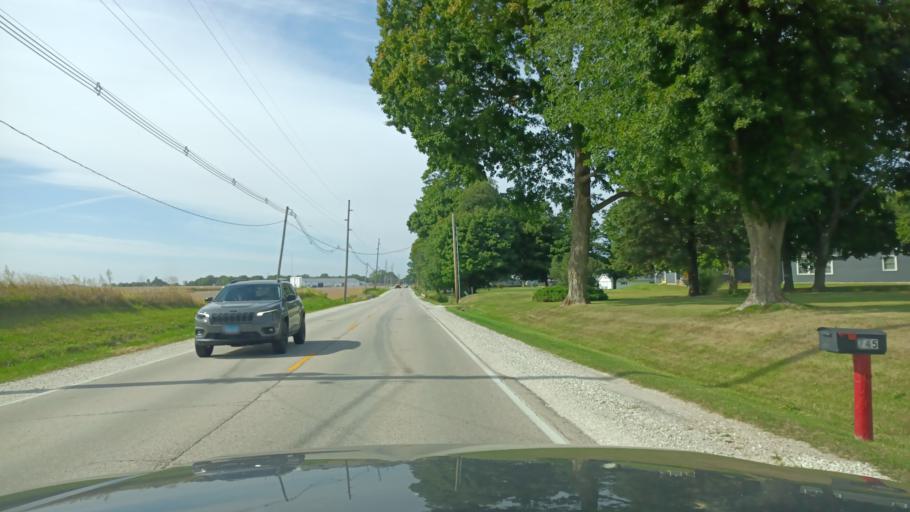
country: US
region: Illinois
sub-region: Knox County
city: Knoxville
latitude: 40.9143
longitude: -90.3011
